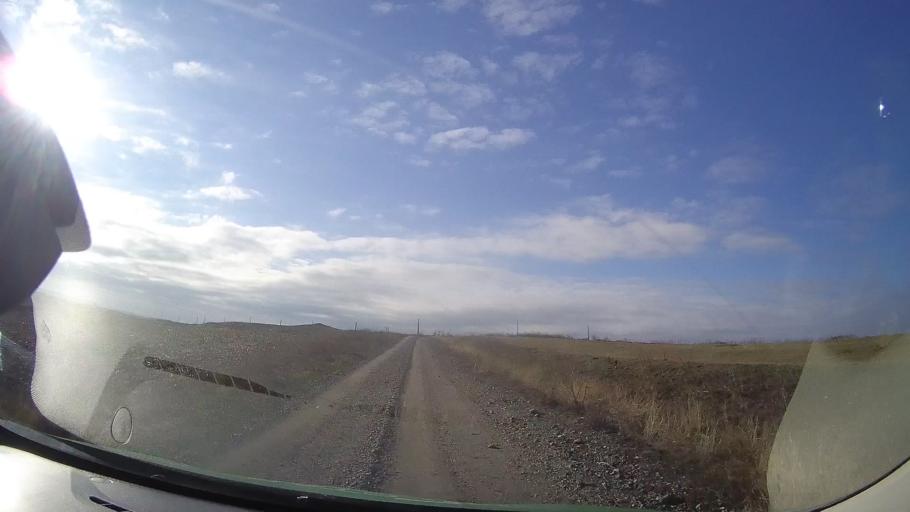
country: RO
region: Mures
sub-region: Comuna Saulia
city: Saulia
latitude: 46.5968
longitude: 24.2214
